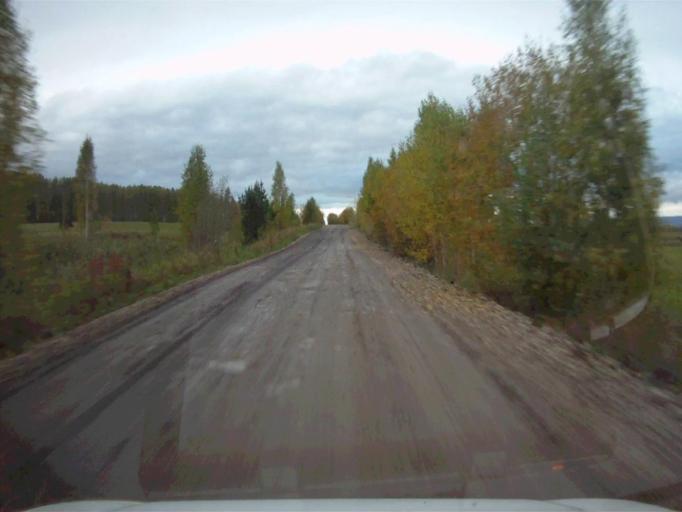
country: RU
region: Sverdlovsk
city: Mikhaylovsk
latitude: 56.1978
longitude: 59.1997
